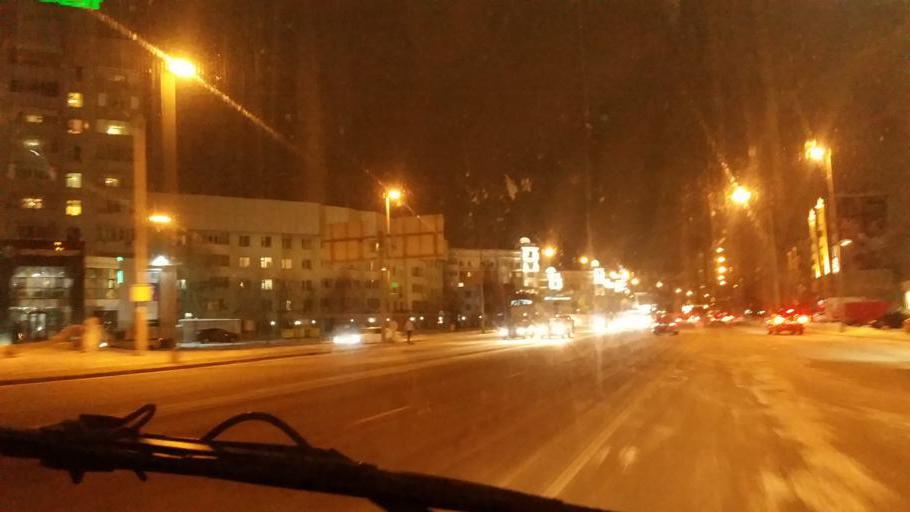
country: KZ
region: Astana Qalasy
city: Astana
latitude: 51.1560
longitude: 71.4342
